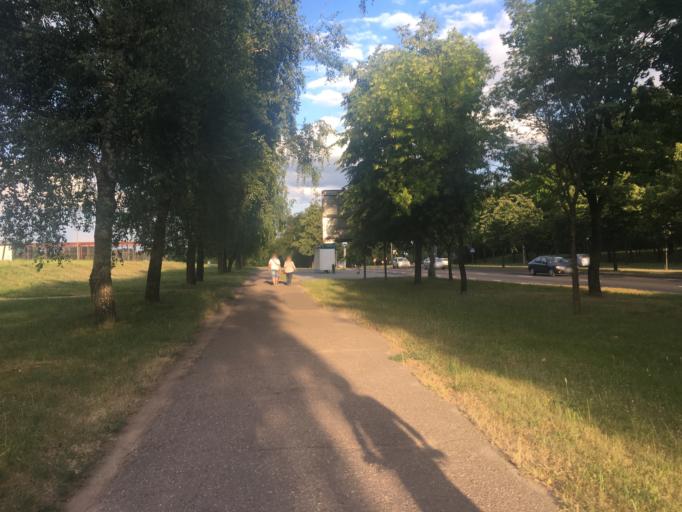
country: BY
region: Grodnenskaya
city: Hrodna
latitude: 53.6841
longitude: 23.8048
